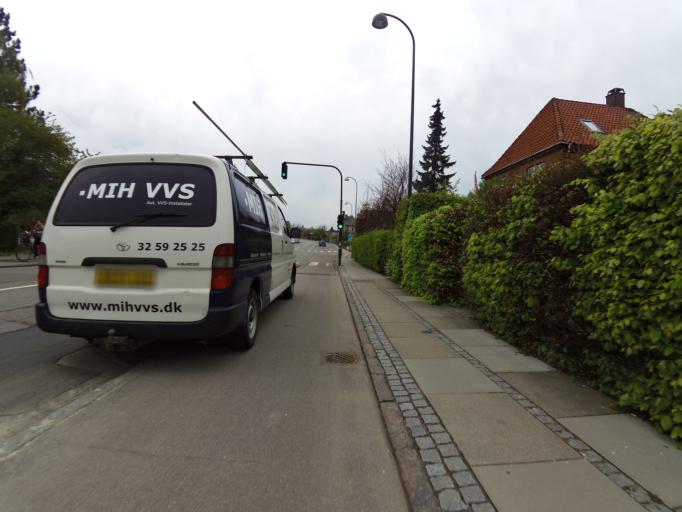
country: DK
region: Capital Region
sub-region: Lyngby-Tarbaek Kommune
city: Kongens Lyngby
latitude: 55.7407
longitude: 12.5182
